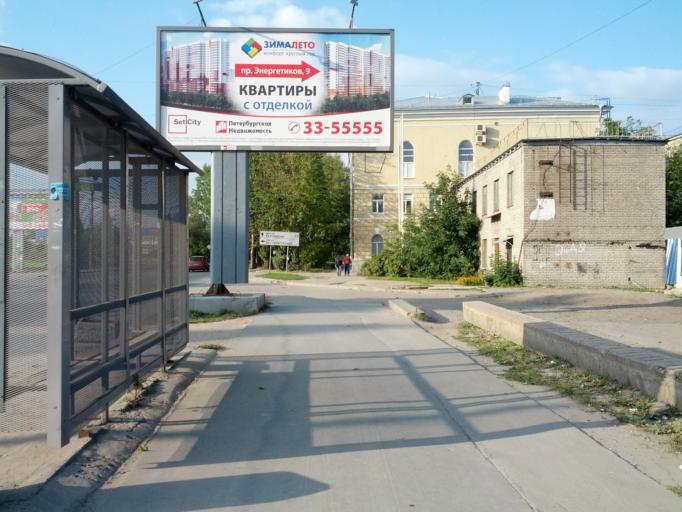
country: RU
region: St.-Petersburg
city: Krasnogvargeisky
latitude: 59.9392
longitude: 30.4353
